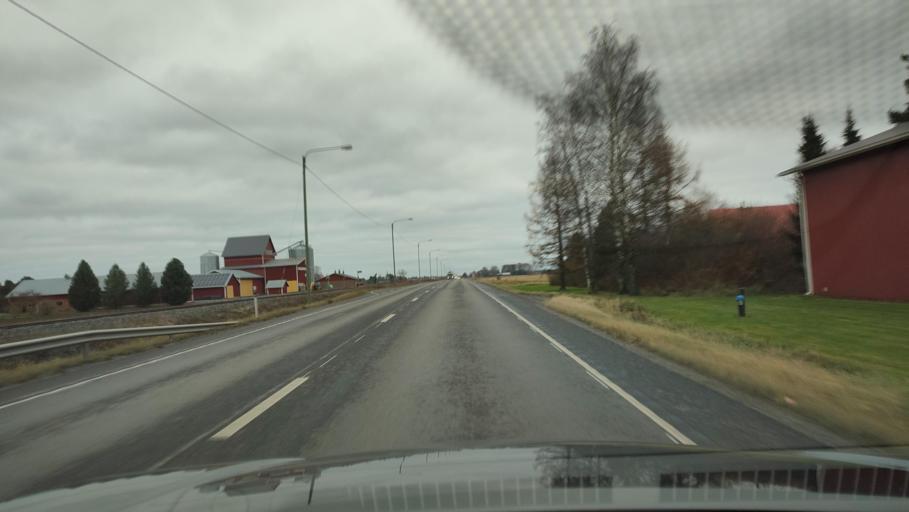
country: FI
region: Southern Ostrobothnia
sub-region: Seinaejoki
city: Ilmajoki
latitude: 62.7074
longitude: 22.5299
